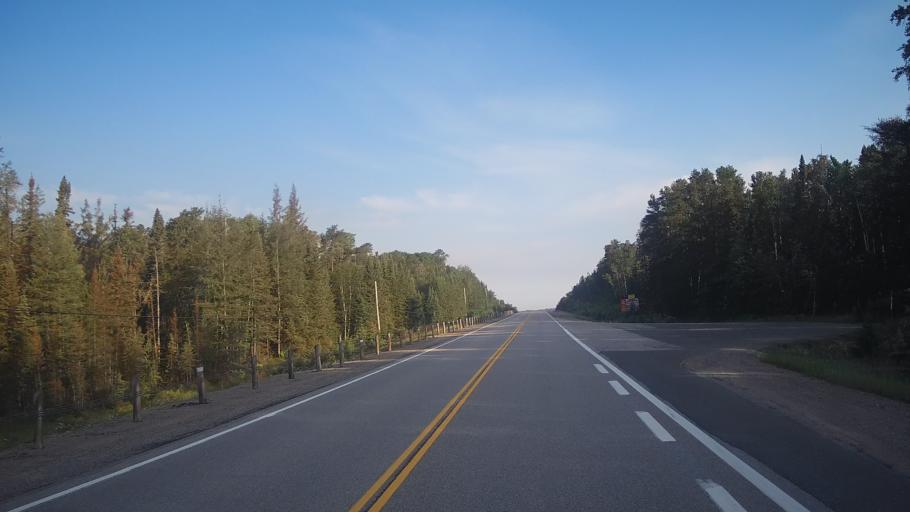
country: CA
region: Ontario
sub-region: Rainy River District
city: Atikokan
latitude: 49.3766
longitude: -91.5794
